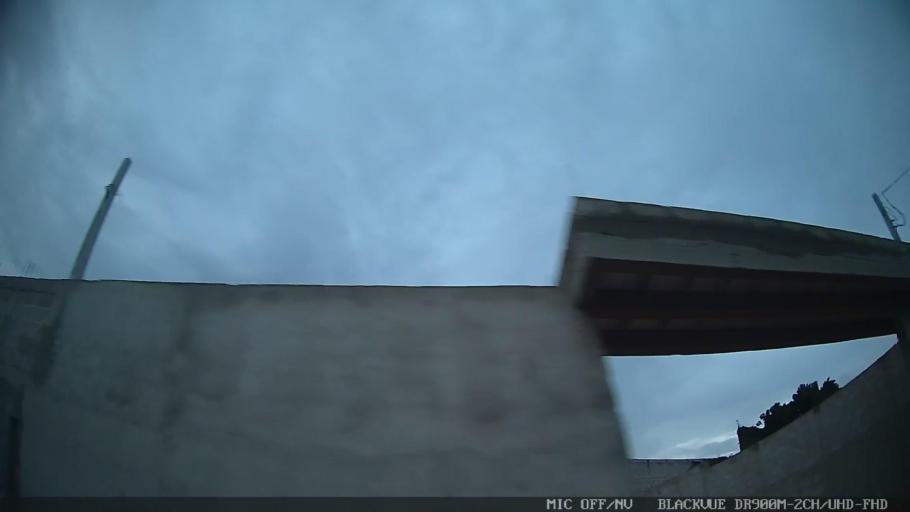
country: BR
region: Sao Paulo
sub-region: Louveira
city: Louveira
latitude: -23.1202
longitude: -46.9636
